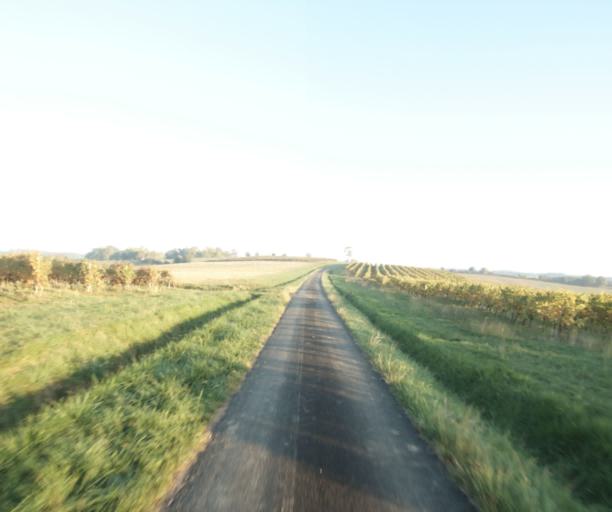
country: FR
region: Midi-Pyrenees
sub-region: Departement du Gers
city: Gondrin
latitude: 43.7777
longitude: 0.1866
